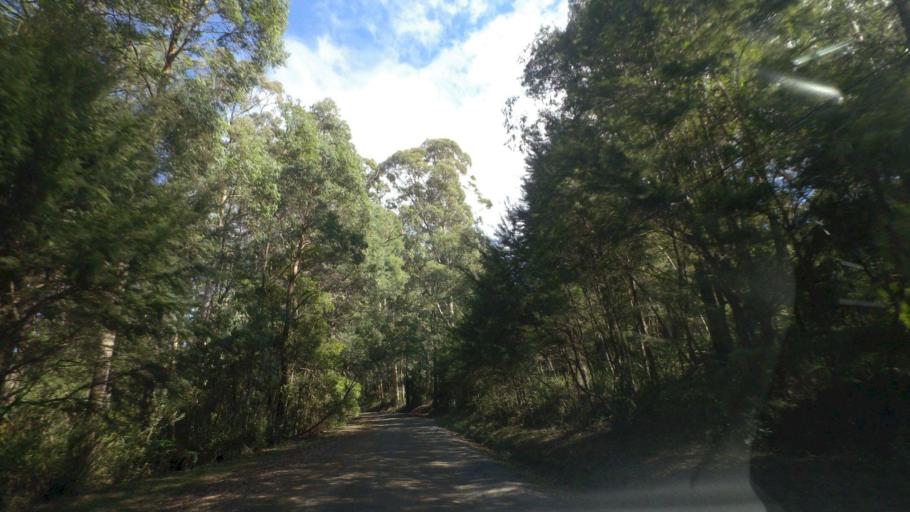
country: AU
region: Victoria
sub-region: Cardinia
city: Gembrook
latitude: -37.9292
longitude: 145.5940
